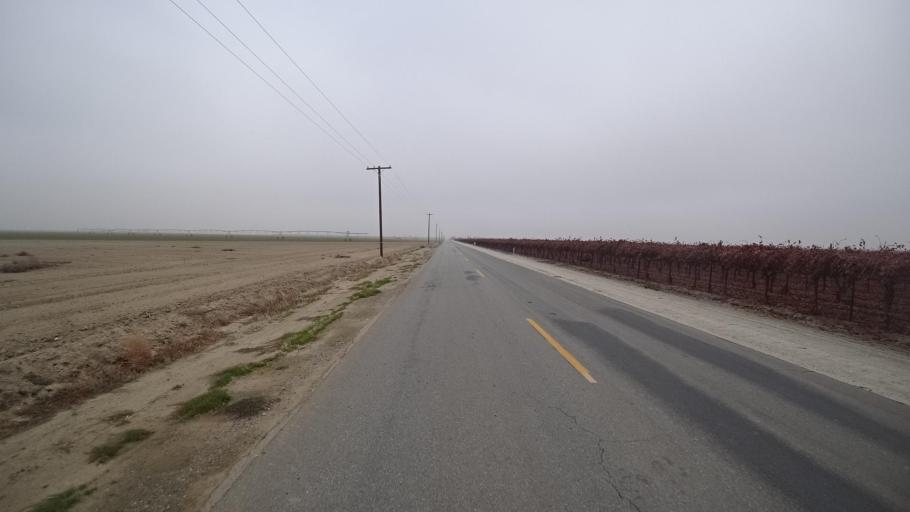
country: US
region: California
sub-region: Kern County
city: Greenfield
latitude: 35.0944
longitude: -119.1265
